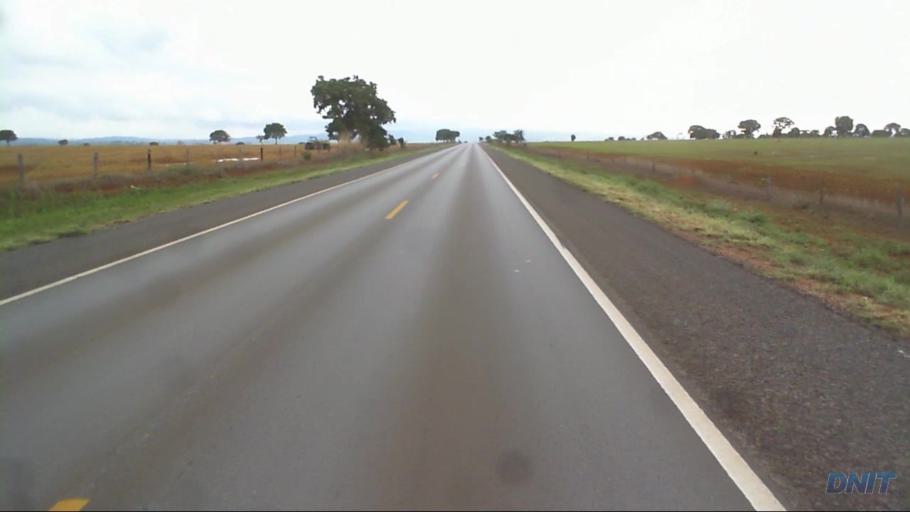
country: BR
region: Goias
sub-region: Padre Bernardo
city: Padre Bernardo
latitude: -15.2176
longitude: -48.6151
